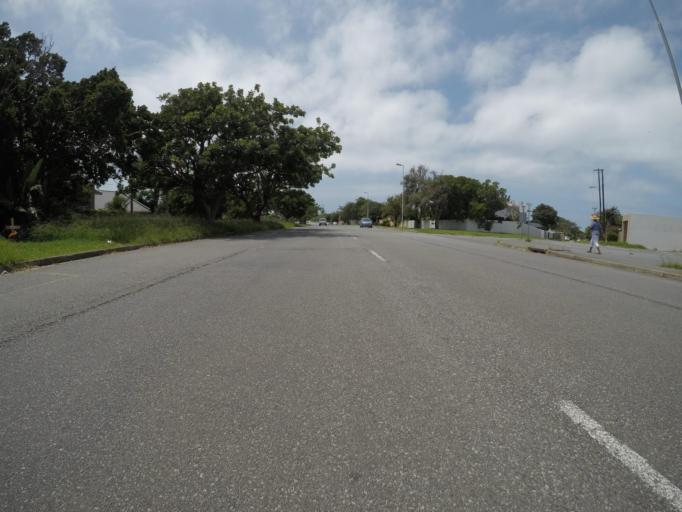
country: ZA
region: Eastern Cape
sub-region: Buffalo City Metropolitan Municipality
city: East London
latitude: -32.9389
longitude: 28.0129
